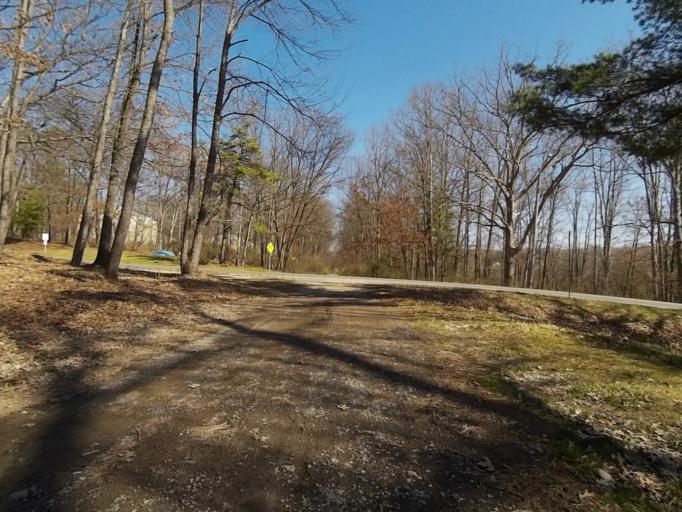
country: US
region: Pennsylvania
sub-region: Centre County
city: Park Forest Village
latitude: 40.8225
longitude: -77.9004
